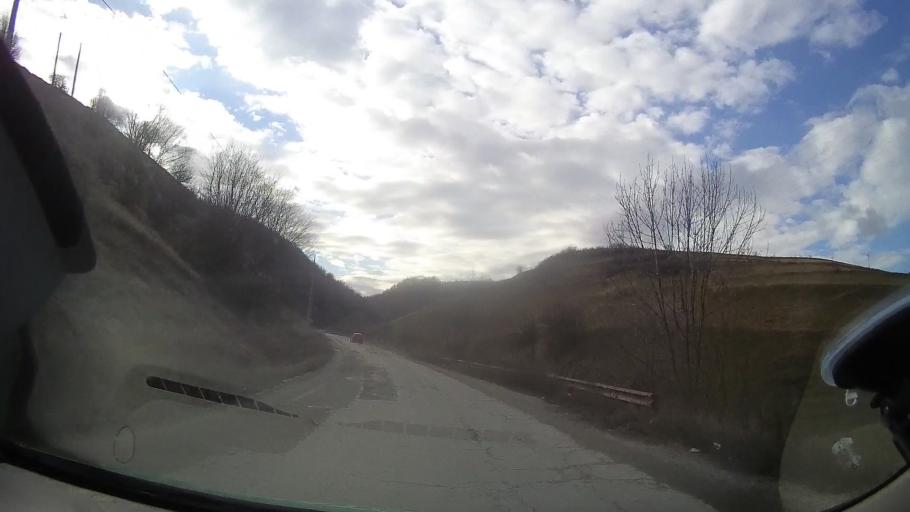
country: RO
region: Cluj
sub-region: Comuna Baisoara
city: Baisoara
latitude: 46.5940
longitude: 23.4605
